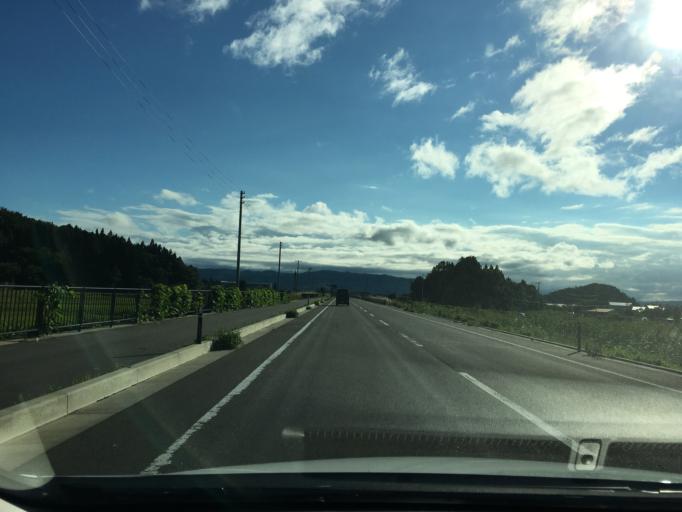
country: JP
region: Yamagata
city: Yonezawa
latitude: 37.9285
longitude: 140.1602
